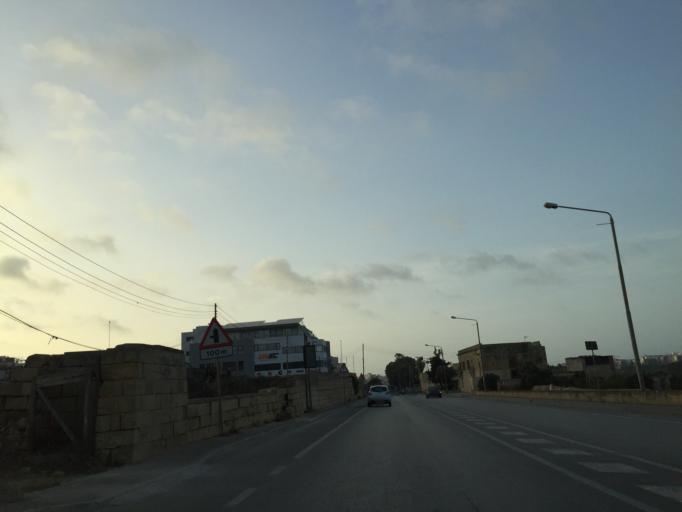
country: MT
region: Saint Paul's Bay
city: San Pawl il-Bahar
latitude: 35.9313
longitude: 14.4161
